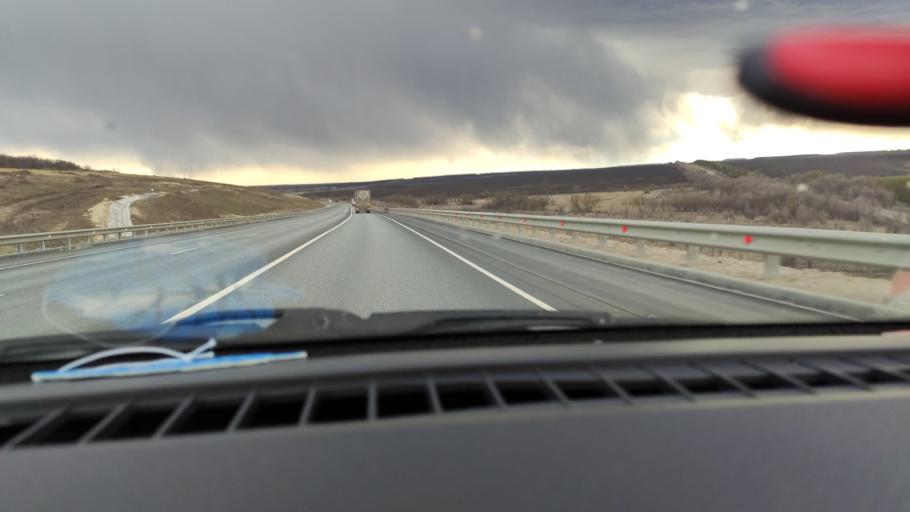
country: RU
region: Saratov
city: Yelshanka
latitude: 51.8738
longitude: 46.5053
